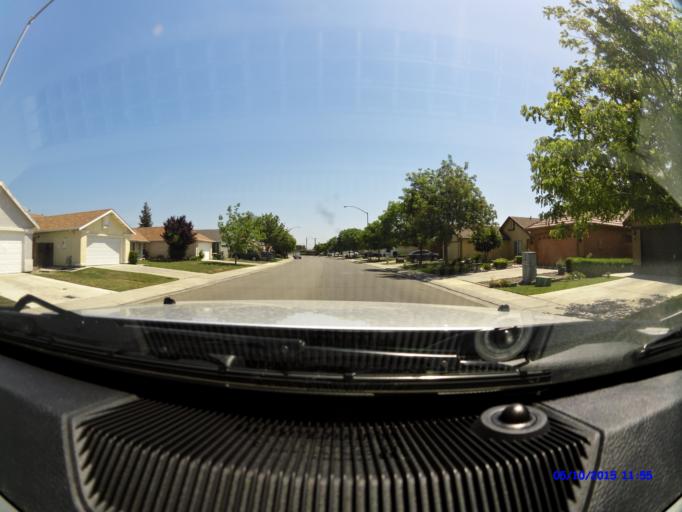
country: US
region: California
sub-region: San Joaquin County
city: Kennedy
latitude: 37.9179
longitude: -121.2317
